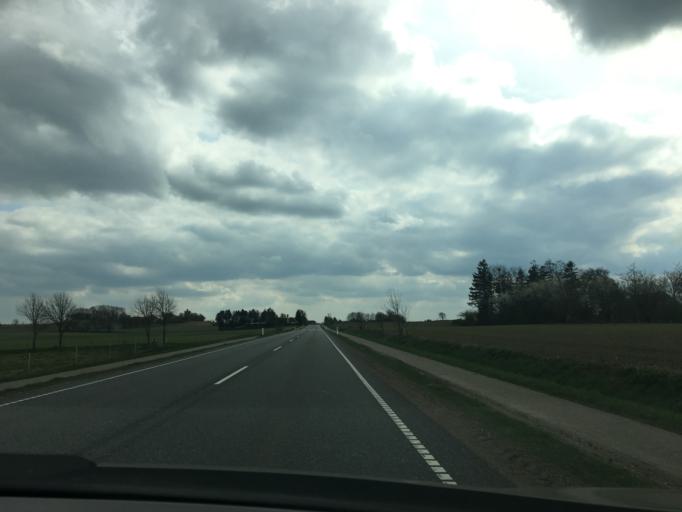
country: DK
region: Central Jutland
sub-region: Horsens Kommune
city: Braedstrup
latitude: 55.9926
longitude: 9.6044
